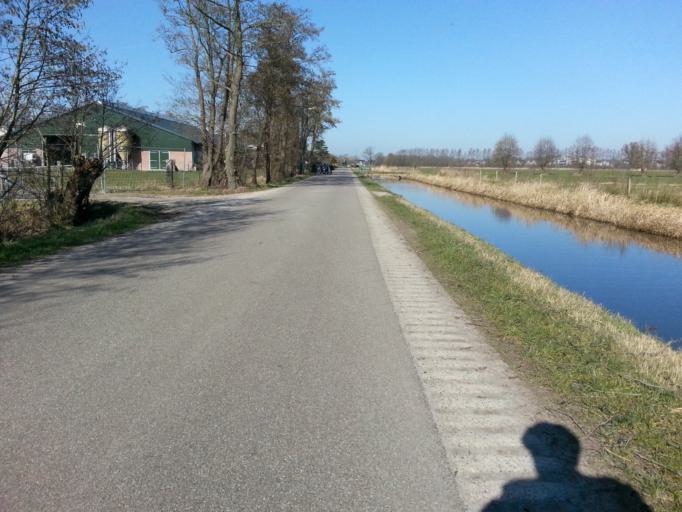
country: NL
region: Utrecht
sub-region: Gemeente Woudenberg
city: Woudenberg
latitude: 52.0724
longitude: 5.4071
